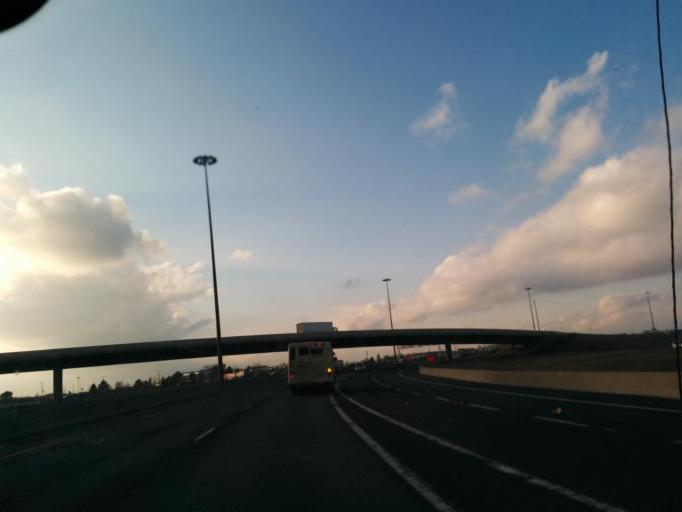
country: CA
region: Ontario
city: Etobicoke
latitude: 43.6716
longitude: -79.5868
